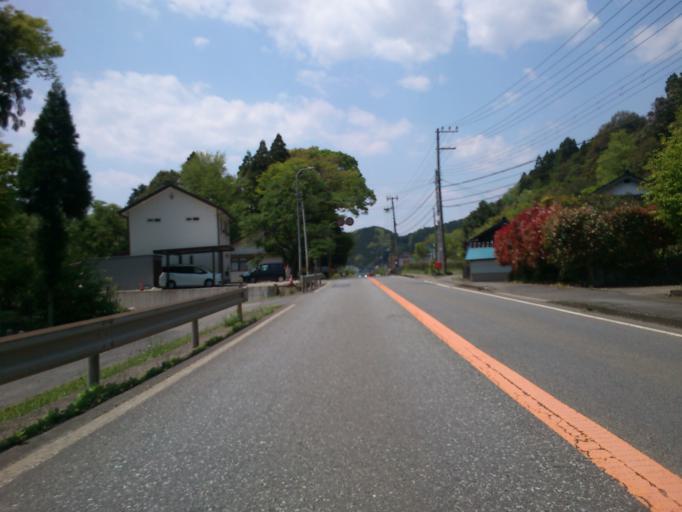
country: JP
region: Kyoto
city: Fukuchiyama
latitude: 35.3236
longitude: 134.9723
